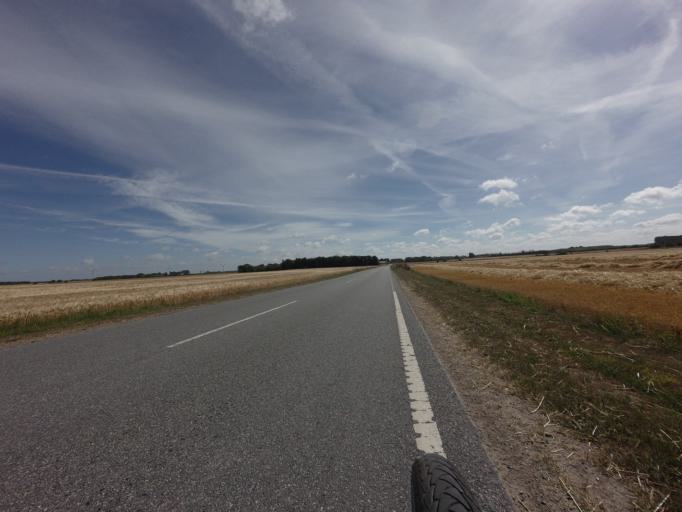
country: DK
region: North Denmark
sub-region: Hjorring Kommune
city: Vra
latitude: 57.3326
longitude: 9.8097
